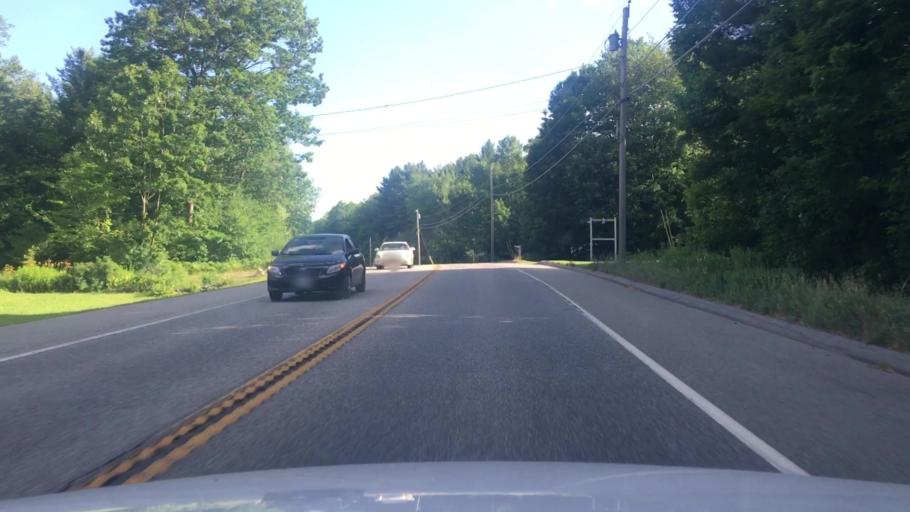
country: US
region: Maine
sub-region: Androscoggin County
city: Livermore
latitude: 44.4213
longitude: -70.2206
